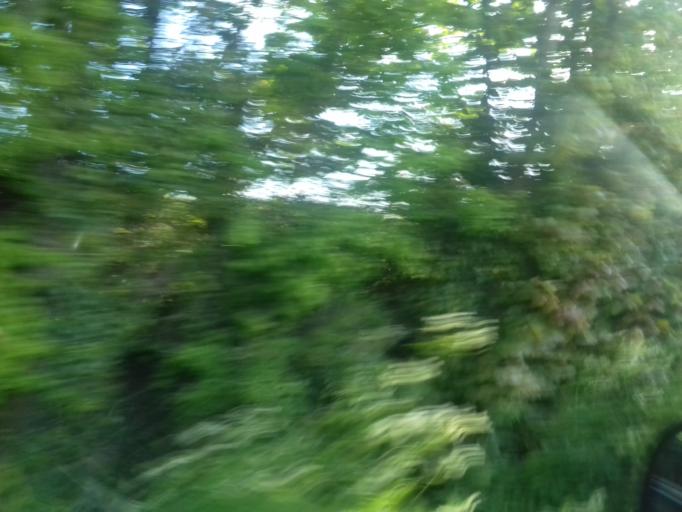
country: IE
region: Leinster
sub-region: Fingal County
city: Blanchardstown
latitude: 53.4254
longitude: -6.3522
